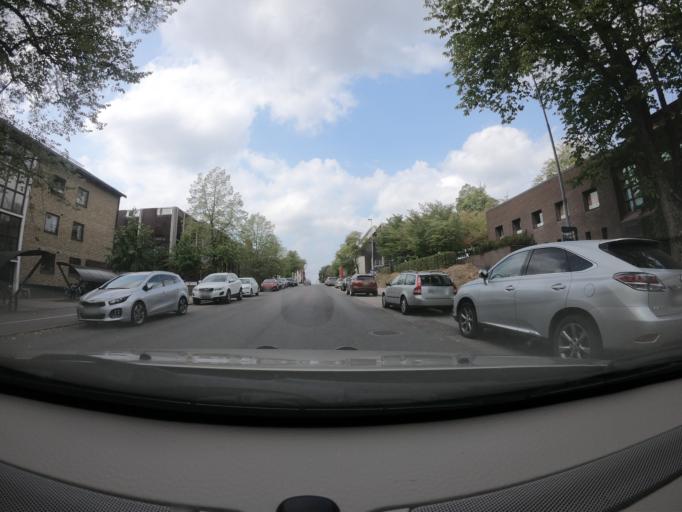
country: SE
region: Kronoberg
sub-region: Vaxjo Kommun
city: Vaexjoe
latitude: 56.8753
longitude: 14.8089
